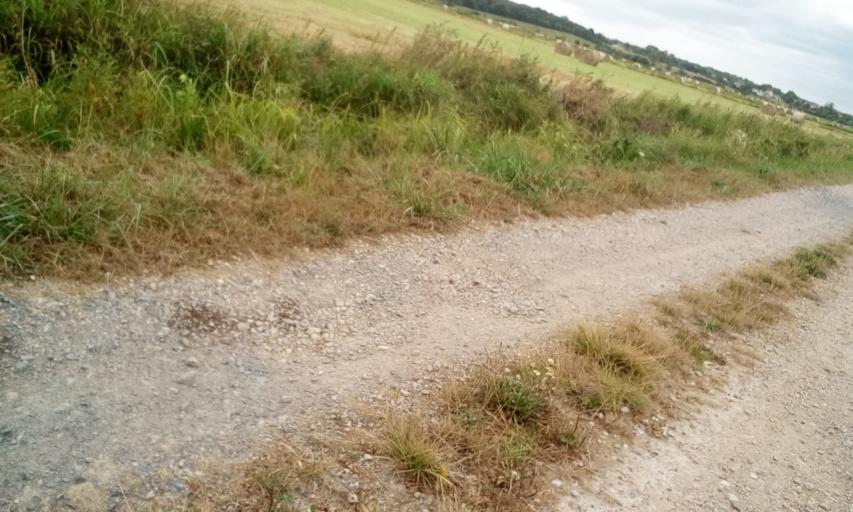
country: FR
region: Lower Normandy
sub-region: Departement du Calvados
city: Troarn
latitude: 49.1871
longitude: -0.1665
